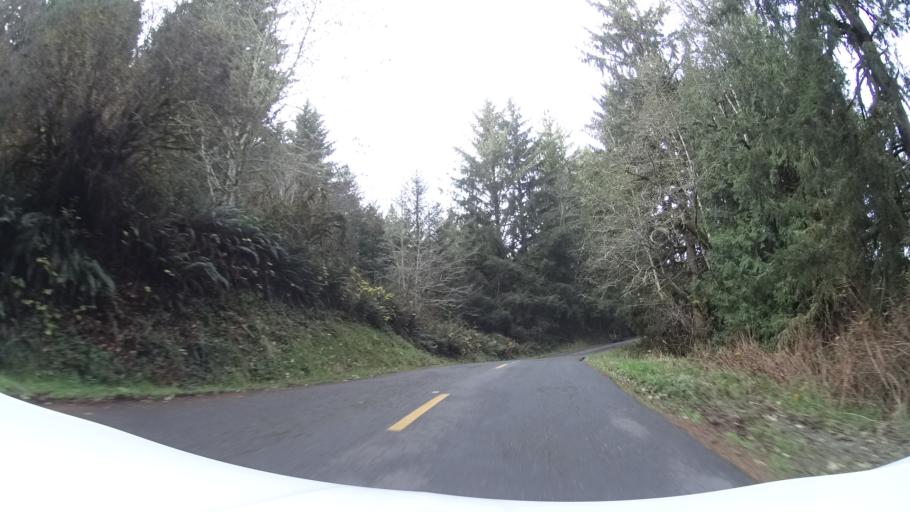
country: US
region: California
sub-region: Humboldt County
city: Ferndale
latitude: 40.5377
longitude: -124.2760
